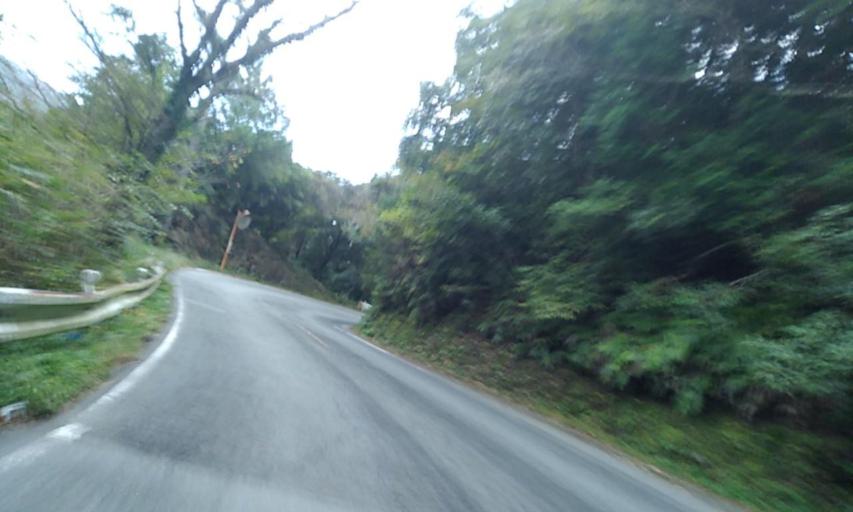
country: JP
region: Mie
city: Ise
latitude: 34.2913
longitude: 136.5331
